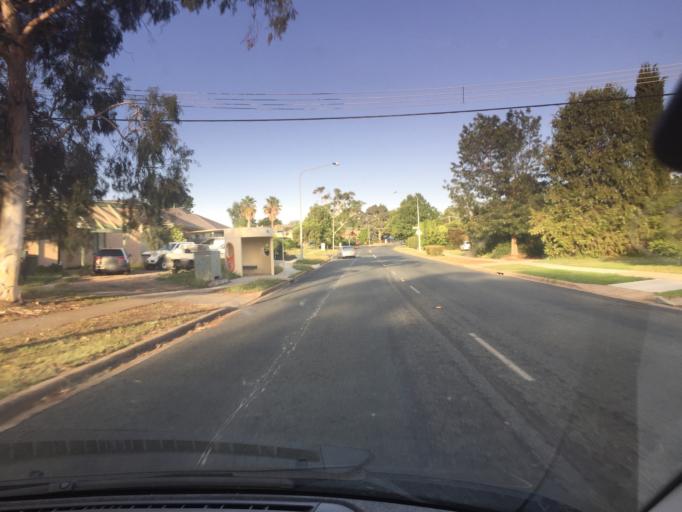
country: AU
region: Australian Capital Territory
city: Kaleen
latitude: -35.2186
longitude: 149.1048
